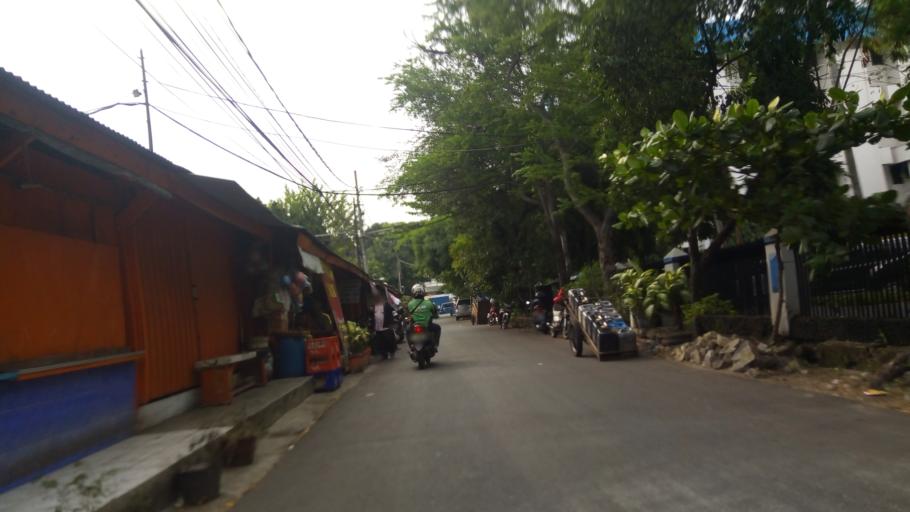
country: ID
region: Jakarta Raya
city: Jakarta
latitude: -6.1685
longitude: 106.8381
